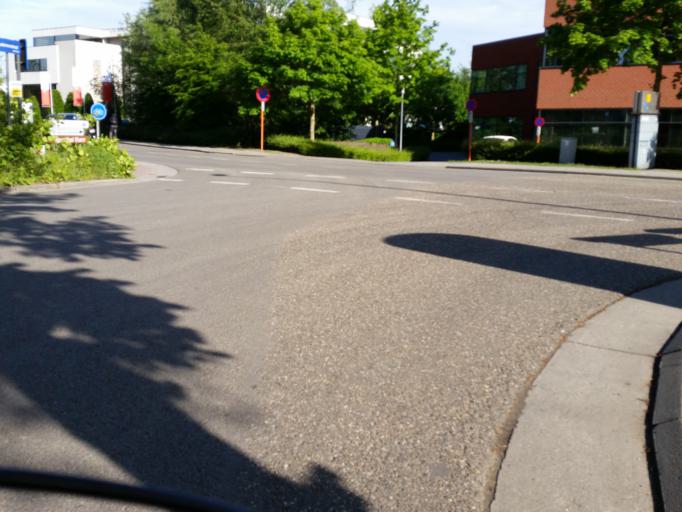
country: BE
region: Flanders
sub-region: Provincie Antwerpen
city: Mechelen
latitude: 51.0142
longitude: 4.4894
